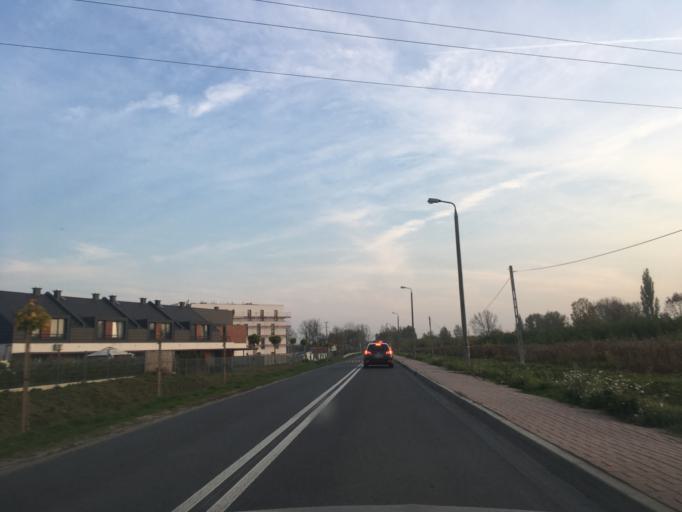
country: PL
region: Masovian Voivodeship
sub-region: Powiat piaseczynski
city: Lesznowola
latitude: 52.0732
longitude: 20.8921
